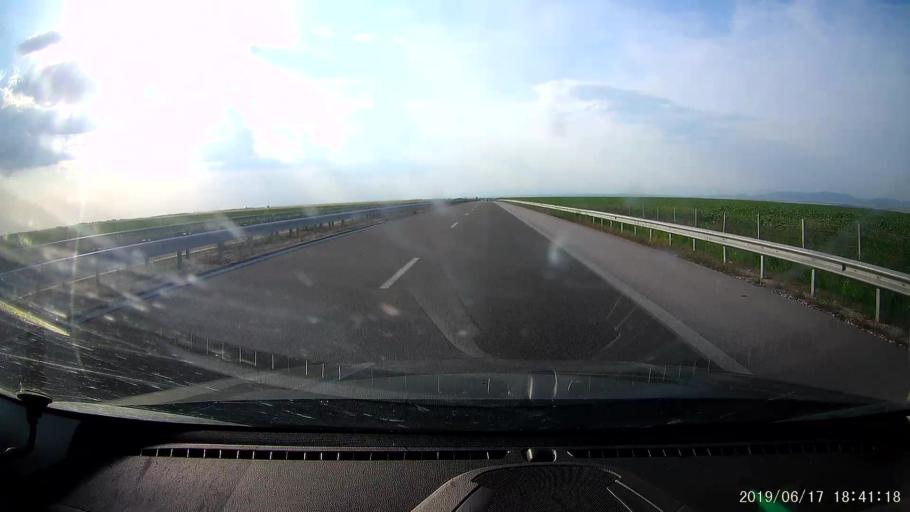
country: BG
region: Stara Zagora
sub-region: Obshtina Chirpan
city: Chirpan
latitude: 42.1699
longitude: 25.2581
